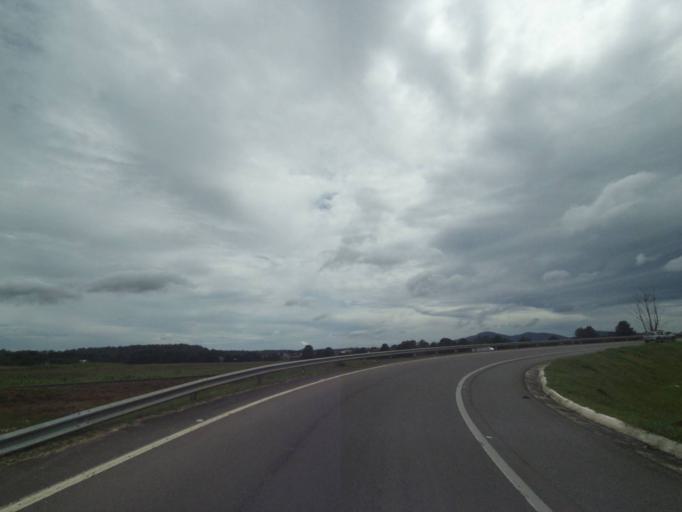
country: BR
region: Parana
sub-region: Piraquara
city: Piraquara
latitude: -25.4609
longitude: -49.0898
